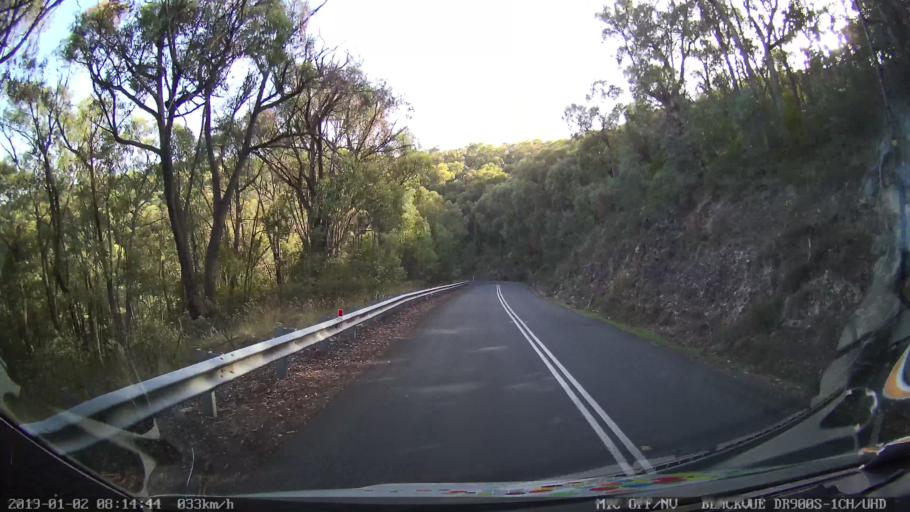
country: AU
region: New South Wales
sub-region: Tumut Shire
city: Tumut
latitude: -35.5851
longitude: 148.3394
